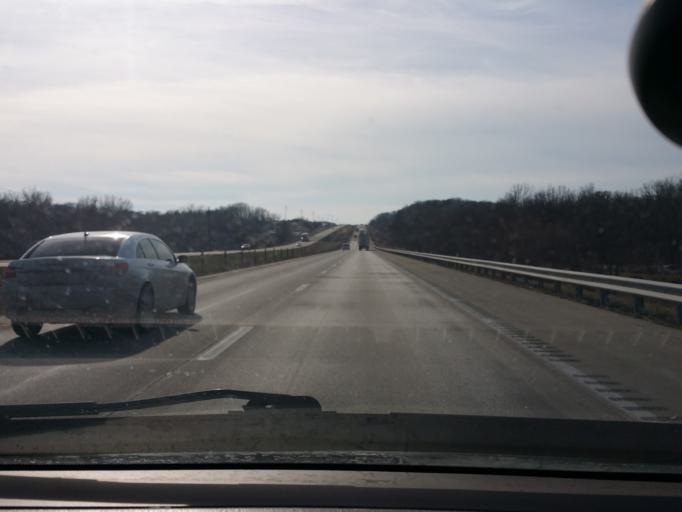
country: US
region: Missouri
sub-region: Clay County
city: Kearney
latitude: 39.3495
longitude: -94.3823
